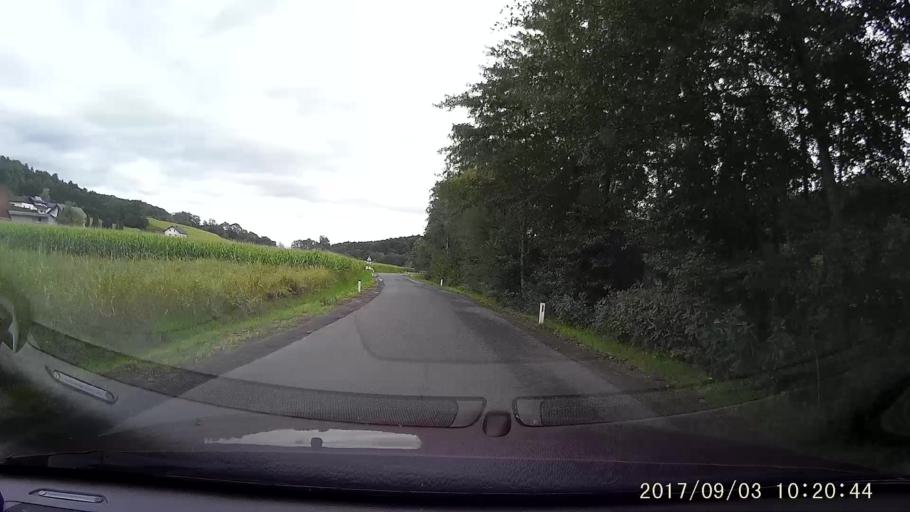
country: AT
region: Styria
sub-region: Politischer Bezirk Suedoststeiermark
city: Breitenfeld an der Rittschein
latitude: 47.0350
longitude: 15.9153
